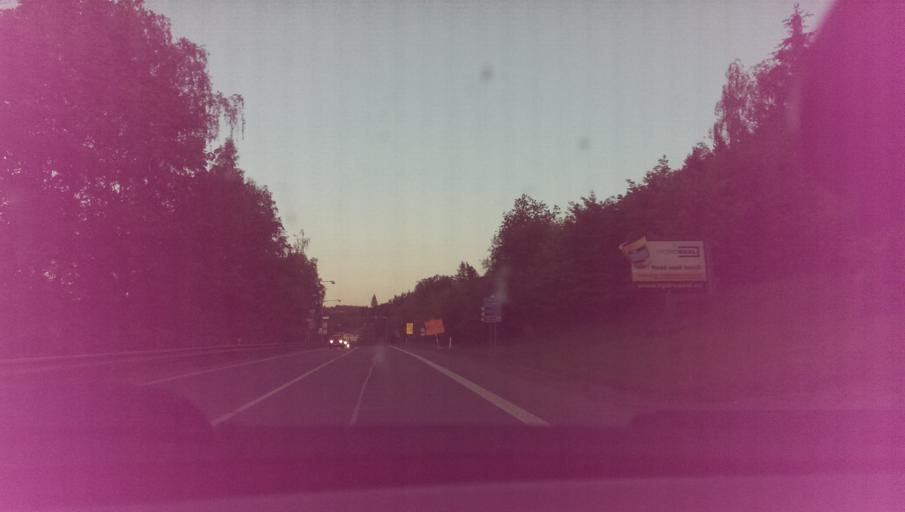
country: CZ
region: Zlin
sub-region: Okres Vsetin
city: Vsetin
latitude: 49.3356
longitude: 17.9823
